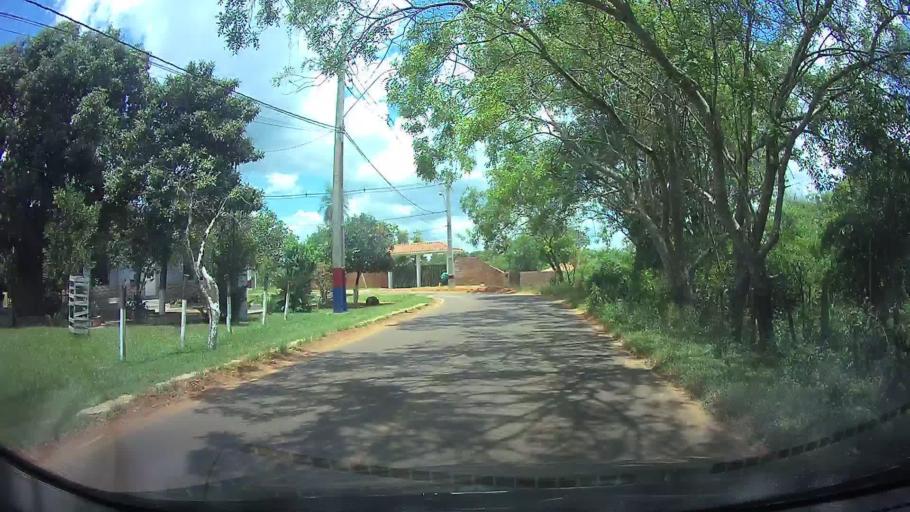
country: PY
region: Central
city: Capiata
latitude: -25.3080
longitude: -57.4370
